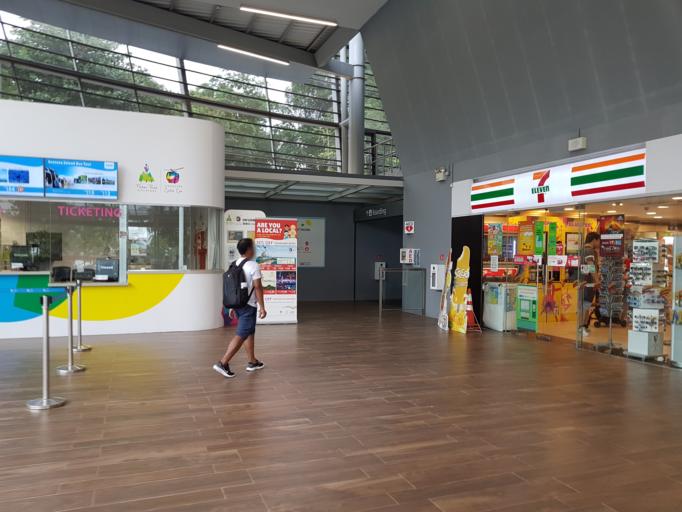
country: SG
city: Singapore
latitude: 1.2573
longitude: 103.8111
